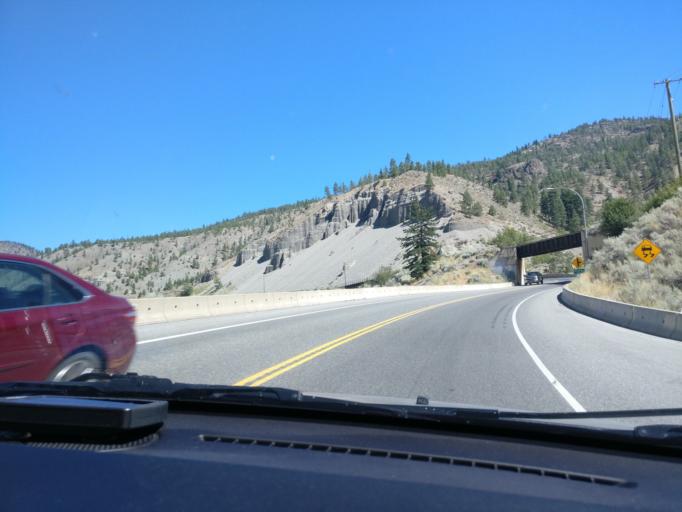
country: CA
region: British Columbia
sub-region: Thompson-Nicola Regional District
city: Ashcroft
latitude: 50.2675
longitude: -121.4028
